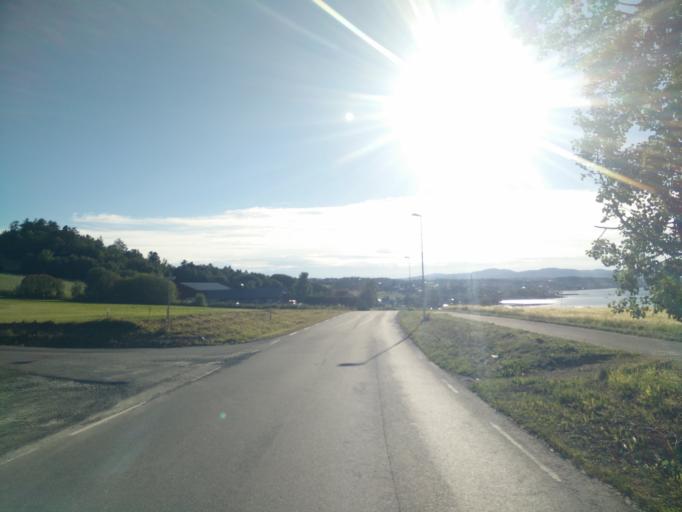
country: NO
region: Sor-Trondelag
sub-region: Malvik
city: Malvik
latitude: 63.4311
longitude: 10.5730
